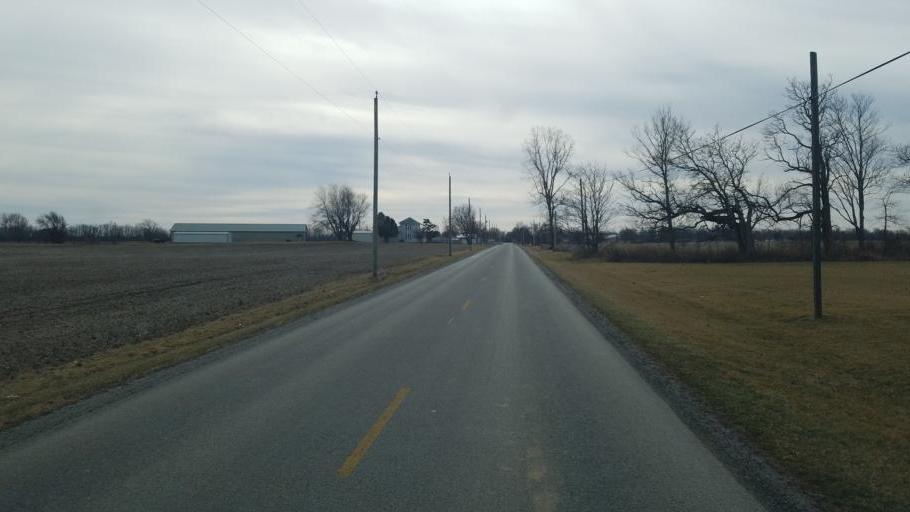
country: US
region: Ohio
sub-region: Hardin County
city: Kenton
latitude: 40.5453
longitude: -83.5144
